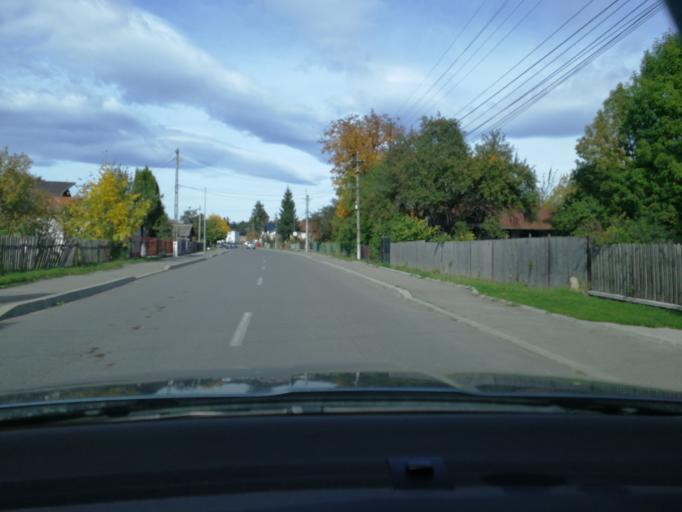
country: RO
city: Brebu Manastirei
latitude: 45.1784
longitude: 25.7687
